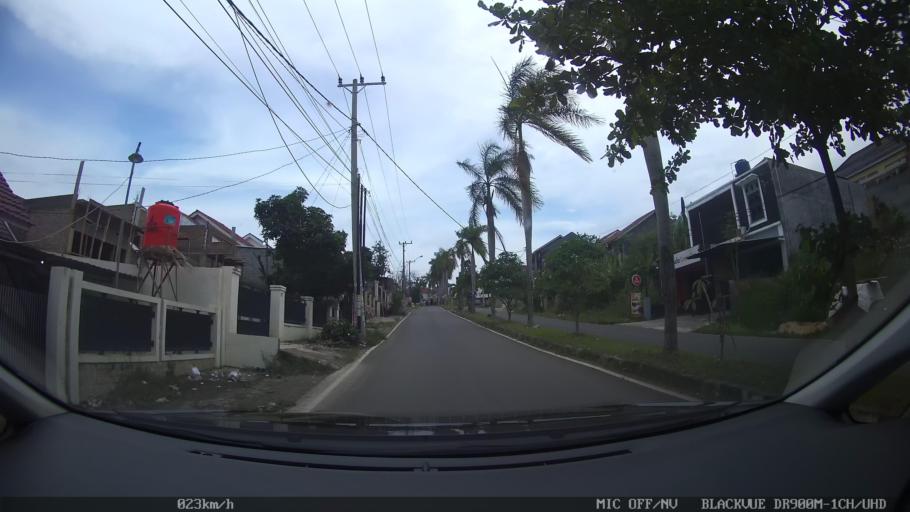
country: ID
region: Lampung
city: Kedaton
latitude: -5.3747
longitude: 105.2130
